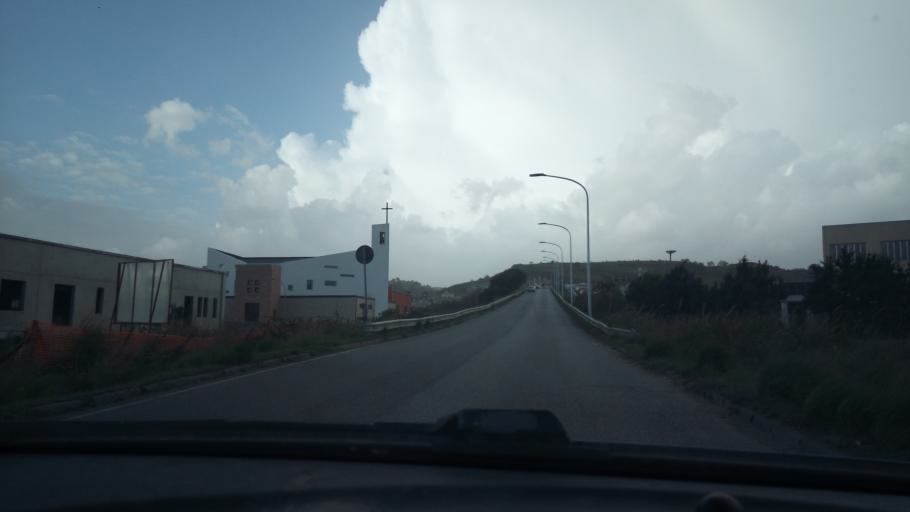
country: IT
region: Calabria
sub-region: Provincia di Catanzaro
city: Barone
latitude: 38.8320
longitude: 16.6391
